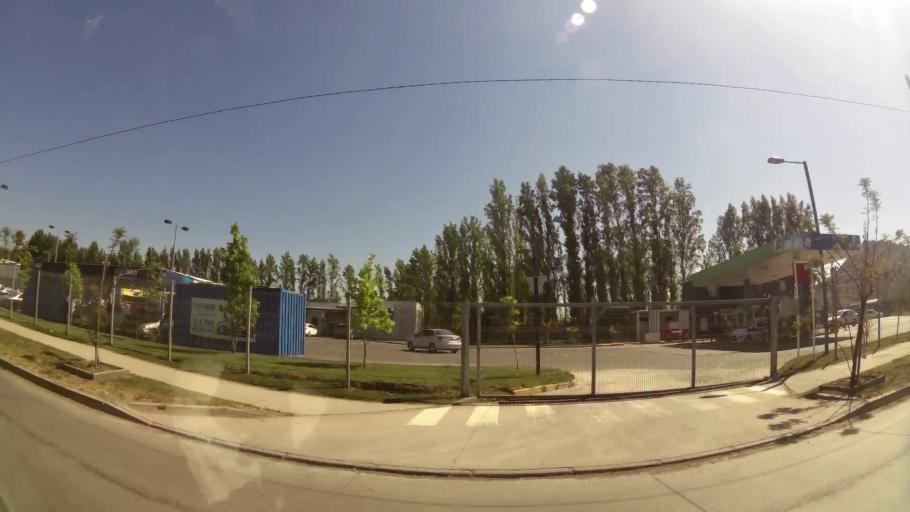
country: CL
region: Santiago Metropolitan
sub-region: Provincia de Maipo
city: San Bernardo
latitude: -33.6161
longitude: -70.6832
